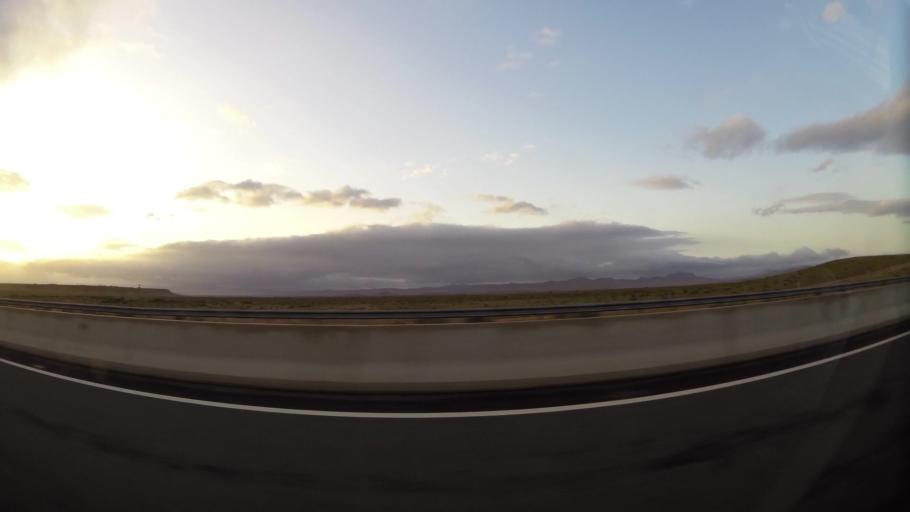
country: MA
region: Oriental
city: Taourirt
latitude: 34.5493
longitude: -2.8806
